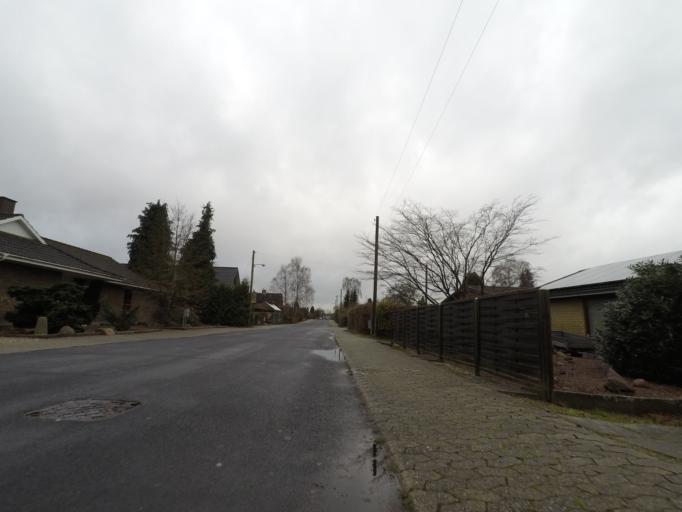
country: DK
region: Capital Region
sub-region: Ballerup Kommune
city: Ballerup
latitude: 55.7486
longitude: 12.3912
